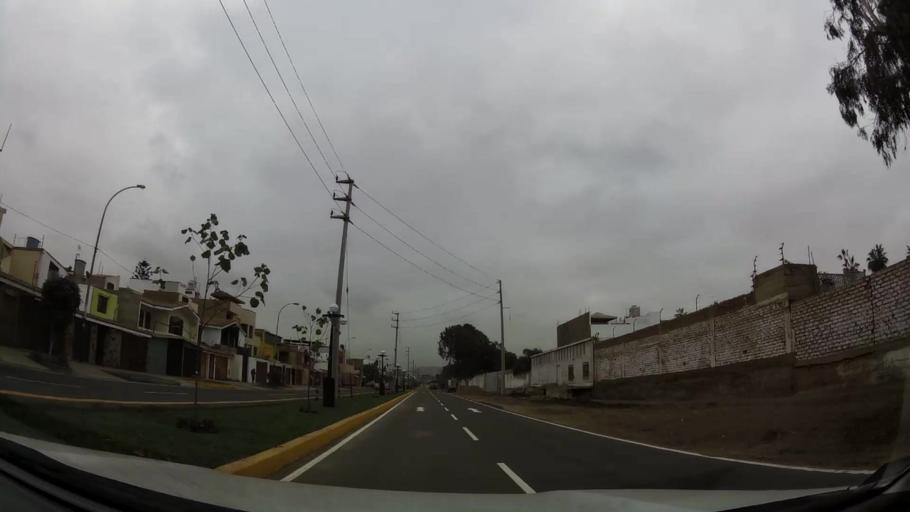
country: PE
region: Lima
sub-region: Lima
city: Surco
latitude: -12.2084
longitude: -77.0125
